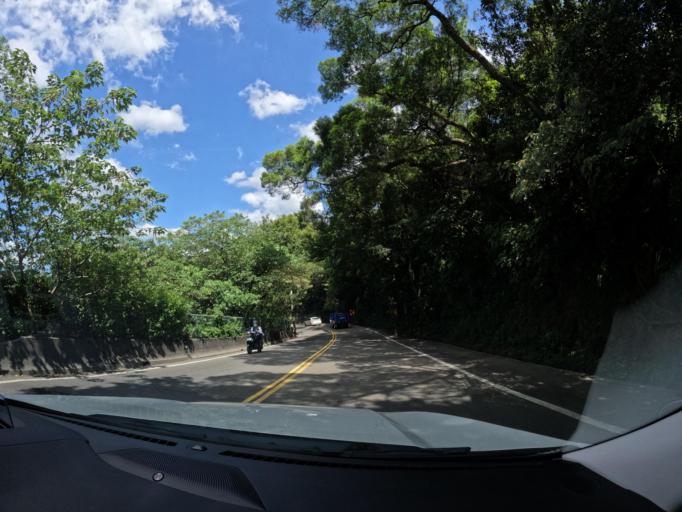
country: TW
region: Taipei
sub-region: Taipei
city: Banqiao
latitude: 25.1155
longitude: 121.3872
